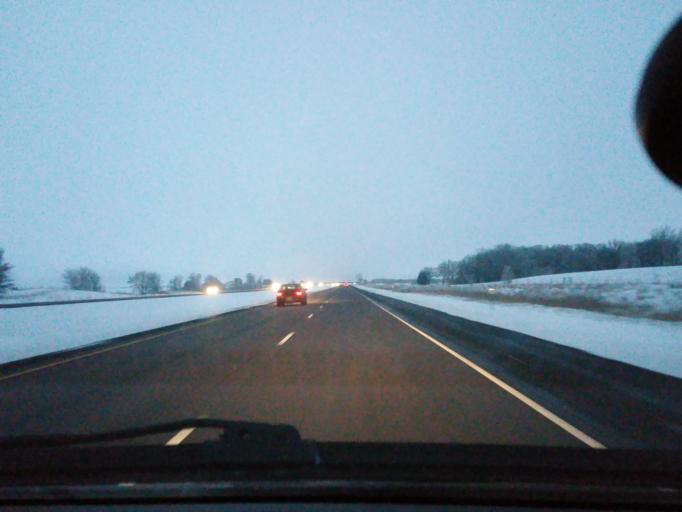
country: US
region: Iowa
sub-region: Worth County
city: Northwood
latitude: 43.4278
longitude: -93.3498
